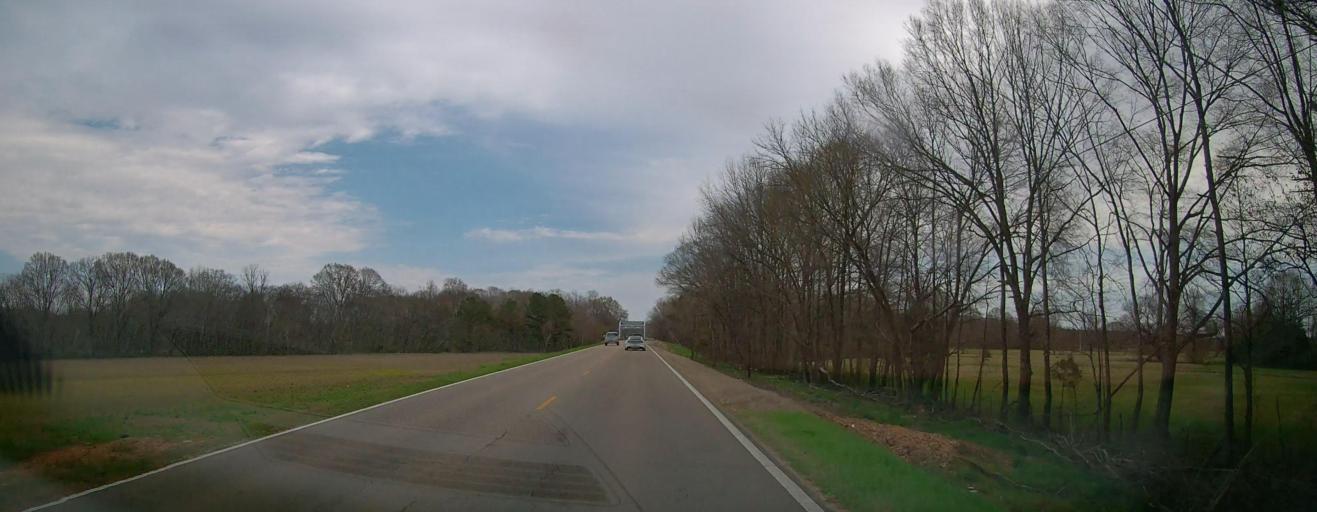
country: US
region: Mississippi
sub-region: Itawamba County
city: Mantachie
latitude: 34.2531
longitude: -88.4797
